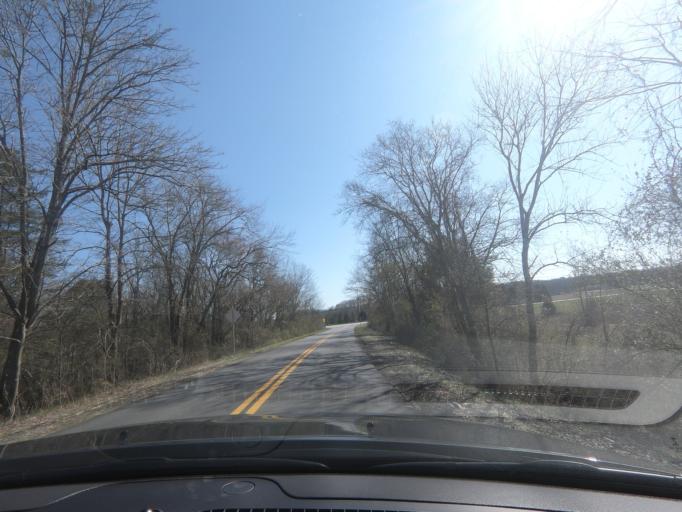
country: US
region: Georgia
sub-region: Gordon County
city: Calhoun
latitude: 34.4615
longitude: -84.9847
